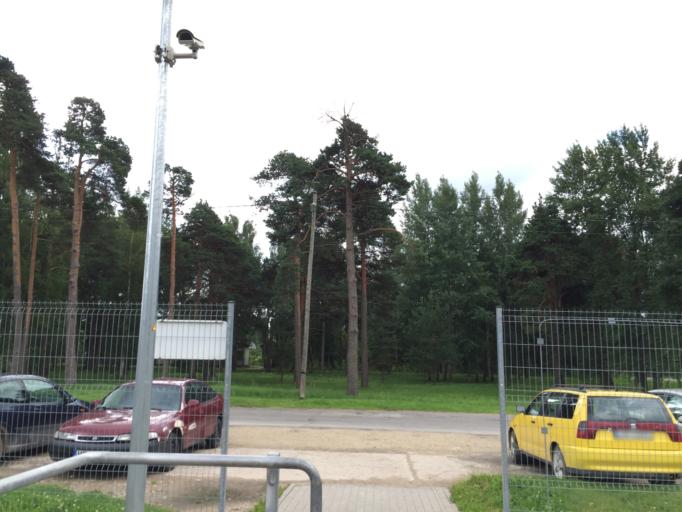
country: LV
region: Sigulda
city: Sigulda
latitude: 57.1532
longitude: 24.8565
